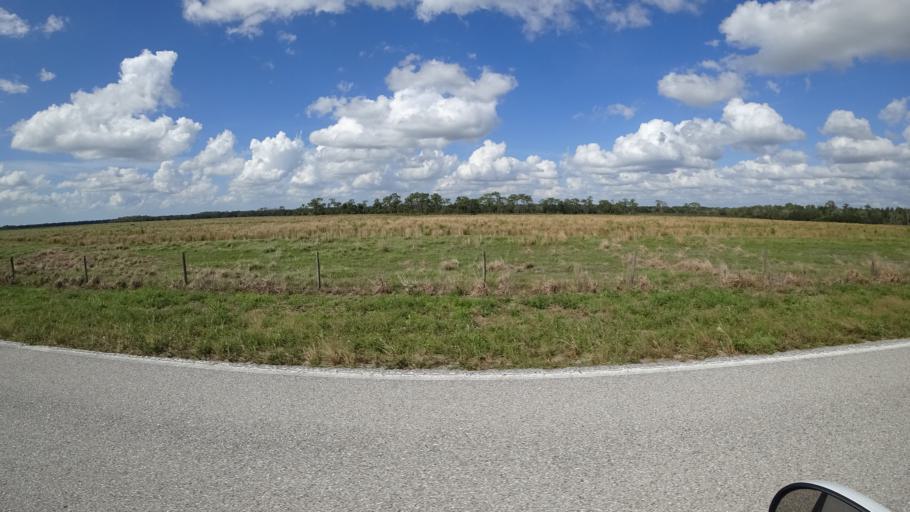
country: US
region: Florida
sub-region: Sarasota County
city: Lake Sarasota
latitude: 27.3187
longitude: -82.1732
